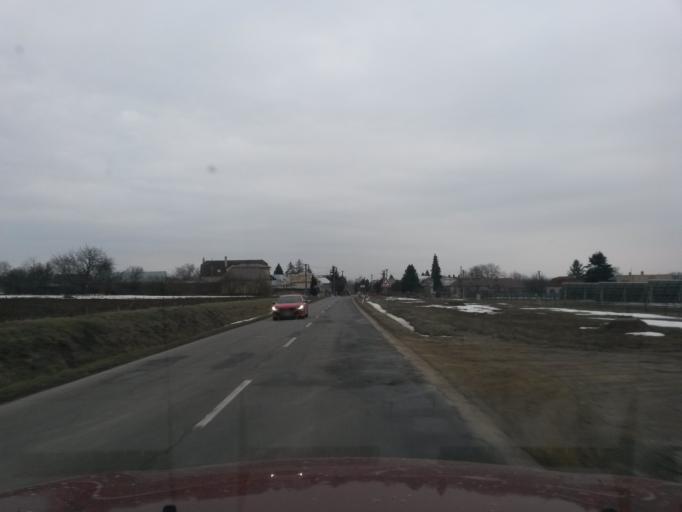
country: SK
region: Kosicky
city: Trebisov
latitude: 48.6900
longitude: 21.8102
